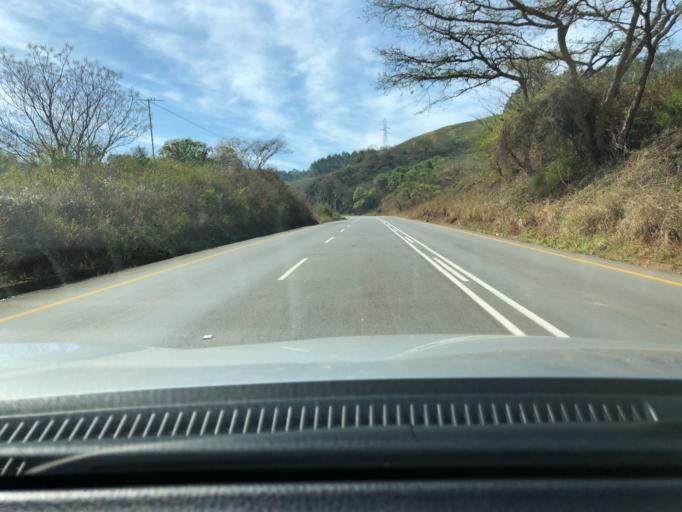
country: ZA
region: KwaZulu-Natal
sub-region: uMgungundlovu District Municipality
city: Richmond
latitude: -29.9283
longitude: 30.2795
